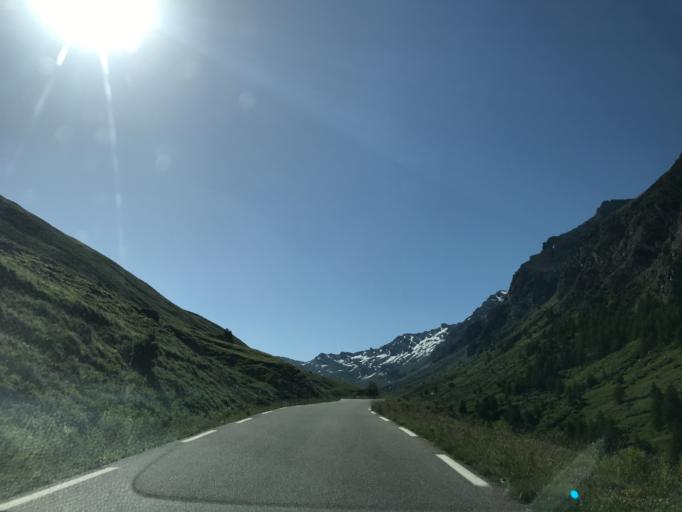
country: IT
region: Piedmont
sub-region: Provincia di Cuneo
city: Pontechianale
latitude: 44.7041
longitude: 6.9339
